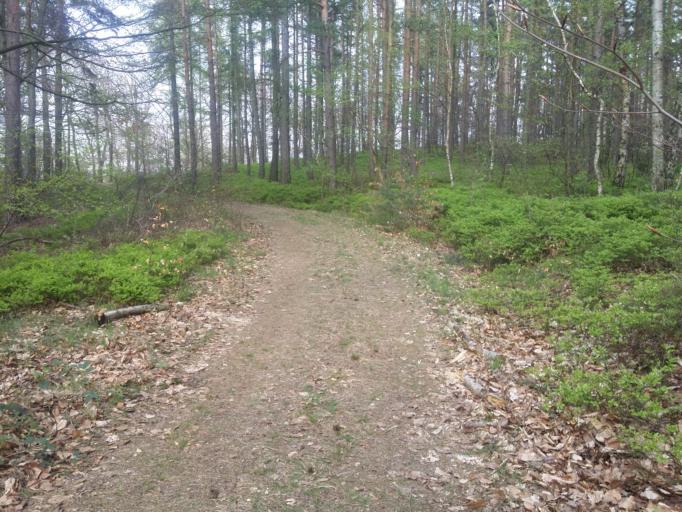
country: DE
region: Saxony-Anhalt
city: Neinstedt
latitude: 51.7236
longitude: 11.0859
